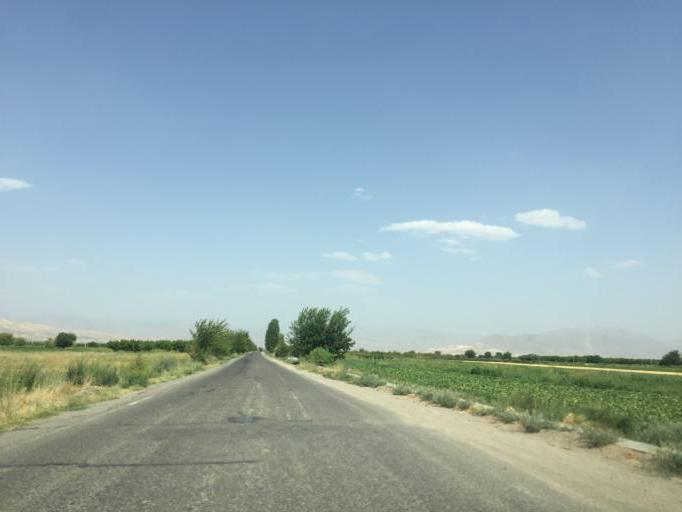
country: AM
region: Ararat
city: Shahumyan
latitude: 39.8827
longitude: 44.5852
